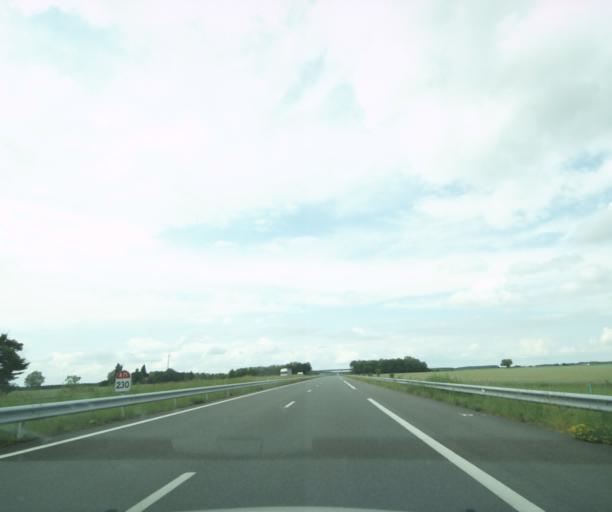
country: FR
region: Centre
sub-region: Departement du Cher
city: Levet
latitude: 46.8907
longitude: 2.4184
